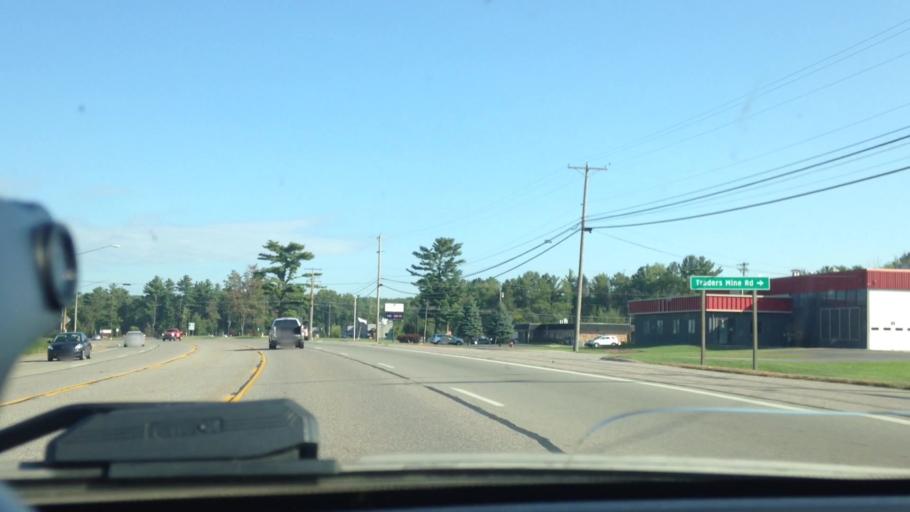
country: US
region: Michigan
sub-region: Dickinson County
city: Iron Mountain
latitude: 45.8435
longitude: -88.0490
